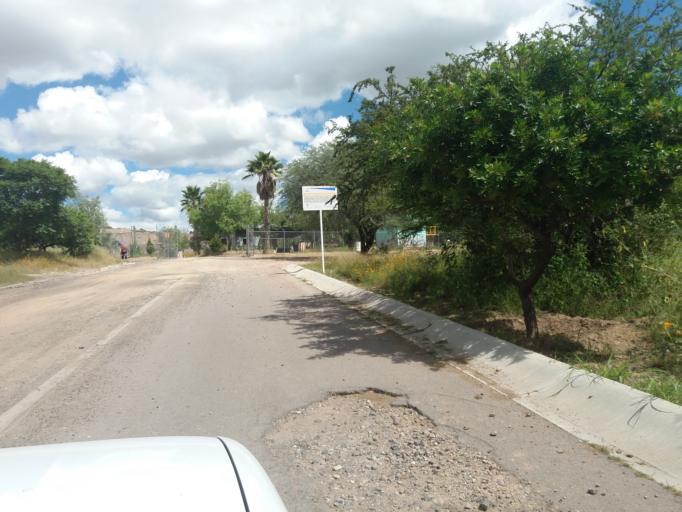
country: MX
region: Aguascalientes
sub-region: Aguascalientes
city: San Sebastian [Fraccionamiento]
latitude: 21.8196
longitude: -102.2606
